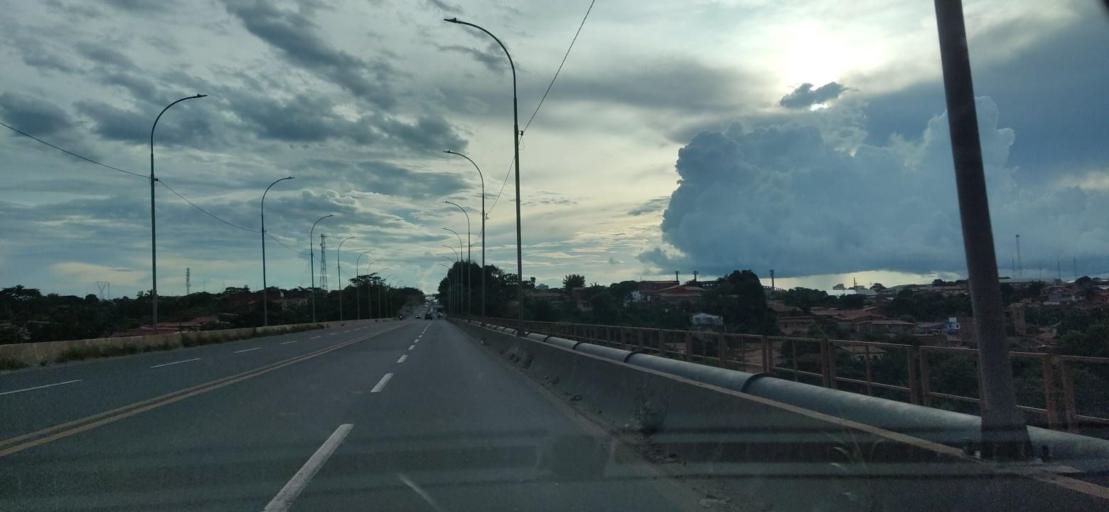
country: BR
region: Piaui
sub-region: Teresina
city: Teresina
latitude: -5.1146
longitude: -42.7781
